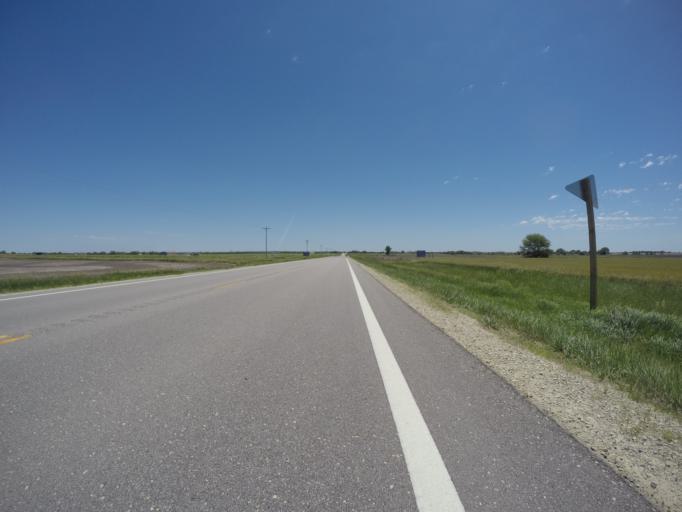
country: US
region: Kansas
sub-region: Republic County
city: Belleville
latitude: 39.8127
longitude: -97.6765
